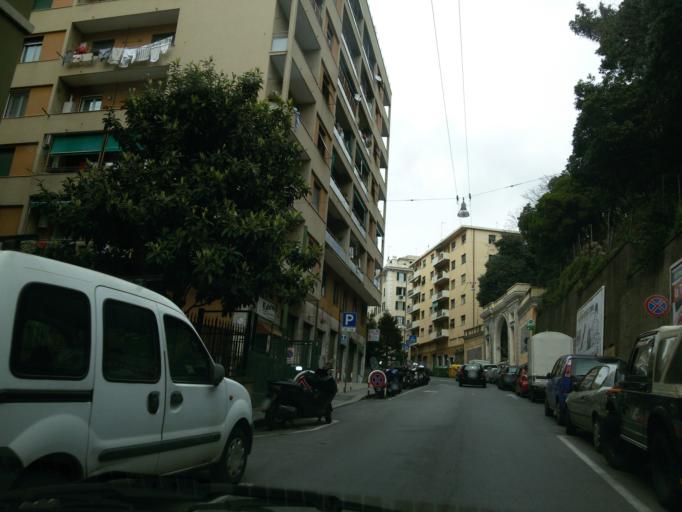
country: IT
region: Liguria
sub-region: Provincia di Genova
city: Genoa
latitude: 44.4097
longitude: 8.9684
